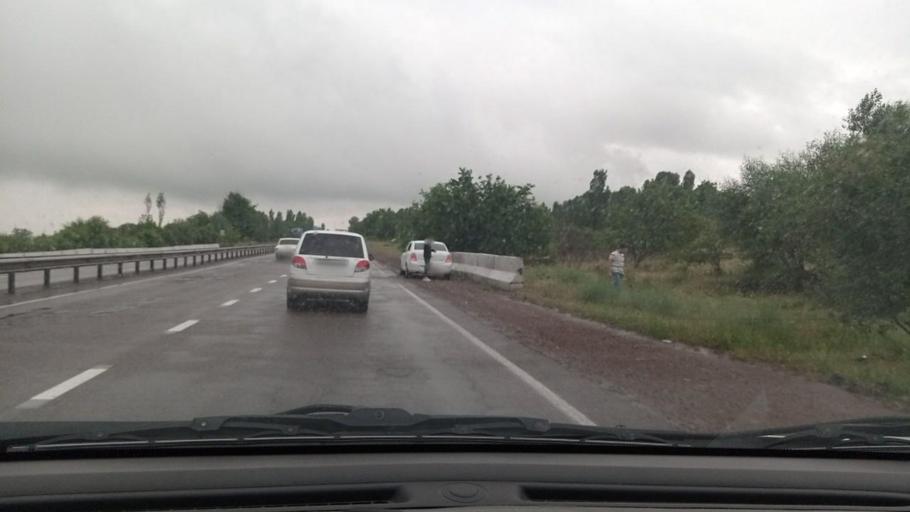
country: UZ
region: Toshkent
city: Ohangaron
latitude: 40.9021
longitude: 69.7107
